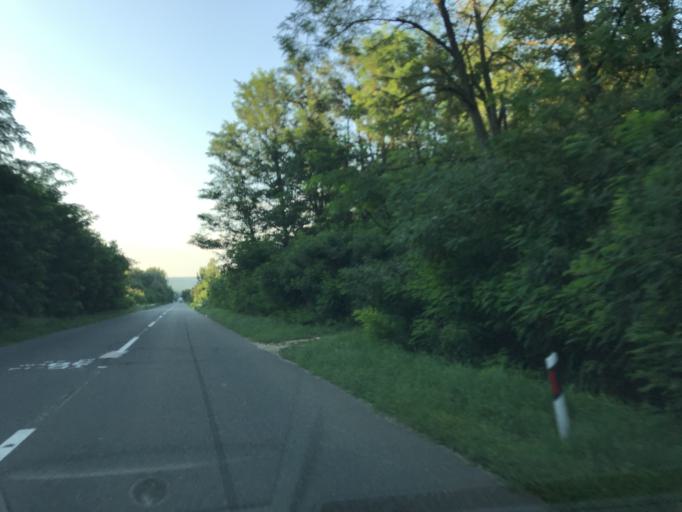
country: RO
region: Mehedinti
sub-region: Comuna Gogosu
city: Ostrovu Mare
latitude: 44.4489
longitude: 22.4538
